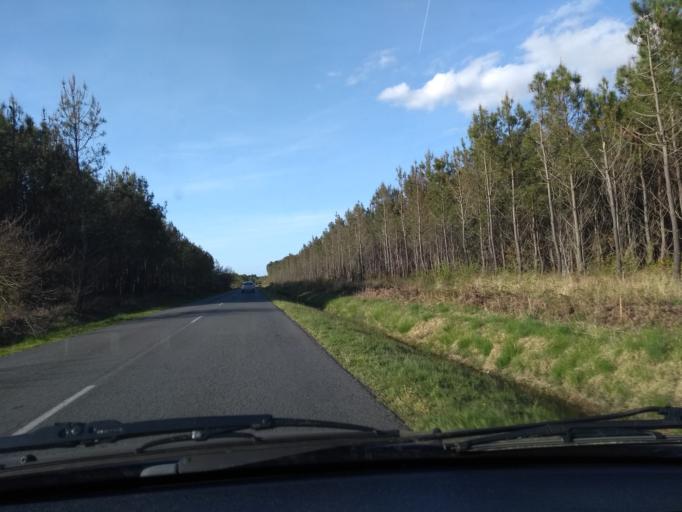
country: FR
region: Aquitaine
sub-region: Departement des Landes
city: Sanguinet
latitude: 44.4587
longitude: -1.0702
